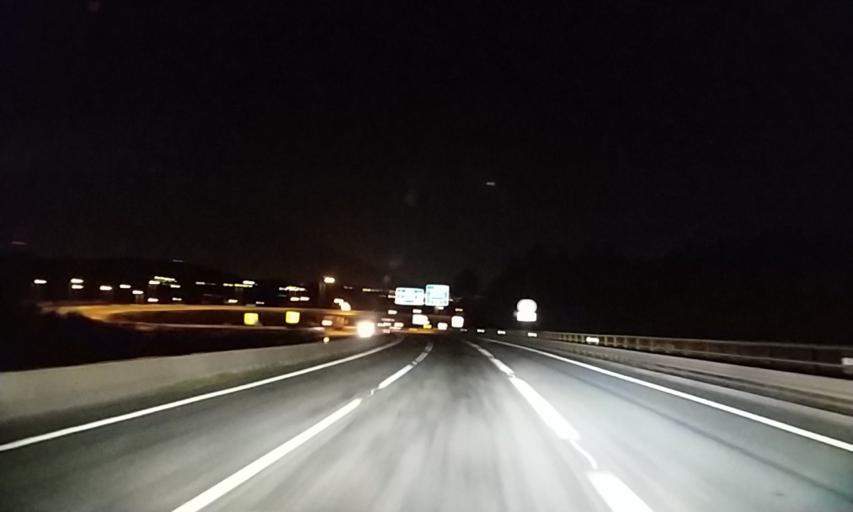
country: PT
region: Porto
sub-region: Vila Nova de Gaia
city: Perozinho
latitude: 41.0818
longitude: -8.5754
